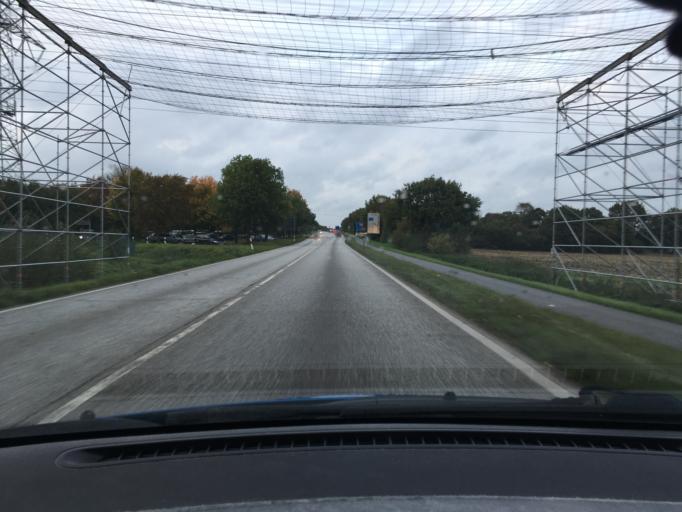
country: DE
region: Schleswig-Holstein
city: Borgstedt
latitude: 54.3428
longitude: 9.6990
